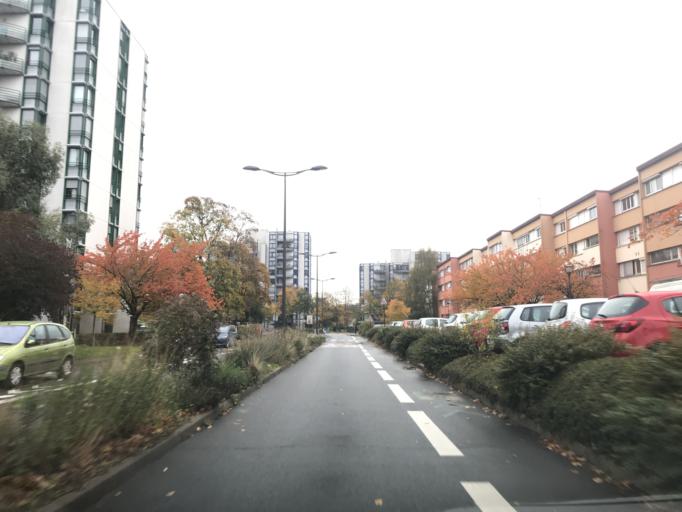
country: FR
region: Ile-de-France
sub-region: Departement de l'Essonne
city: Verrieres-le-Buisson
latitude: 48.7336
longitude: 2.2610
